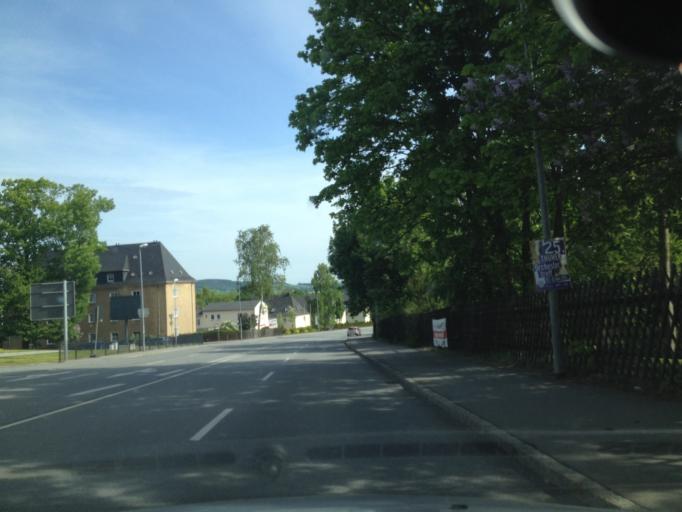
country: DE
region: Saxony
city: Annaberg-Buchholz
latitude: 50.5859
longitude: 13.0149
